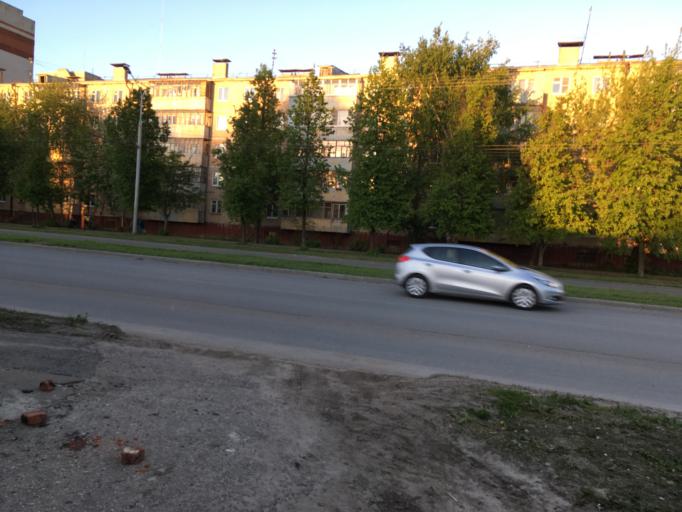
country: RU
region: Mariy-El
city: Yoshkar-Ola
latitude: 56.6309
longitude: 47.9383
